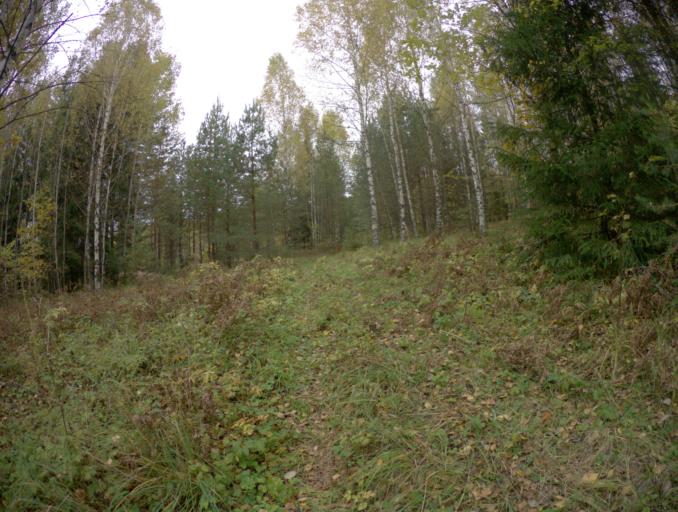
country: RU
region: Vladimir
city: Stepantsevo
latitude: 56.3101
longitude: 41.7313
